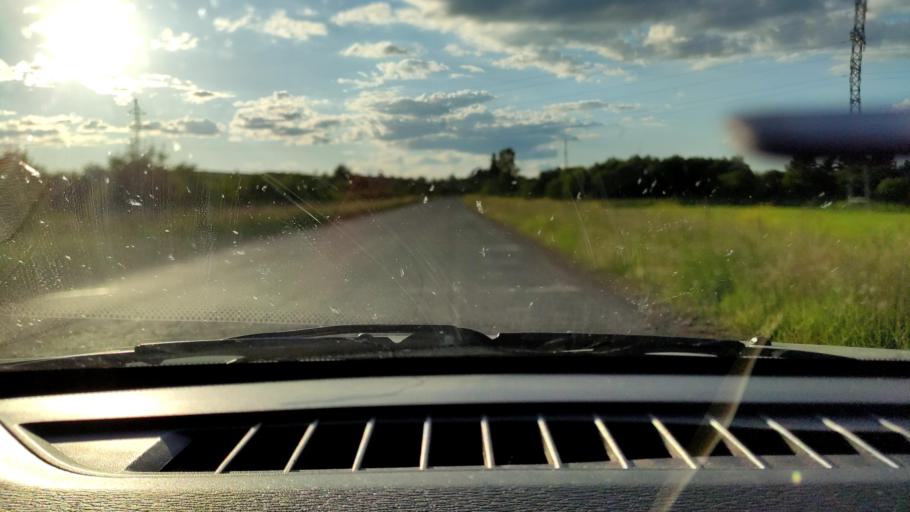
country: RU
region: Perm
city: Uinskoye
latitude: 57.1035
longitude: 56.5371
